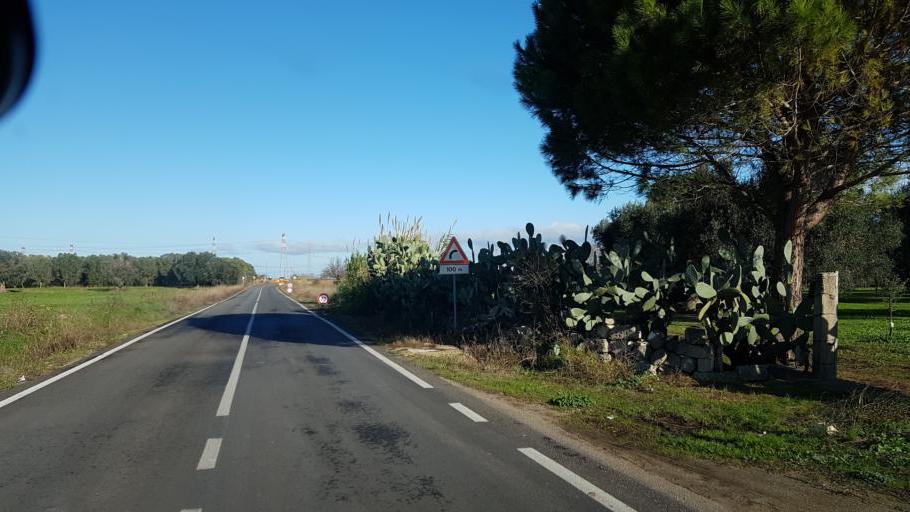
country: IT
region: Apulia
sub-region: Provincia di Brindisi
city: Tuturano
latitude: 40.5504
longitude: 17.9472
